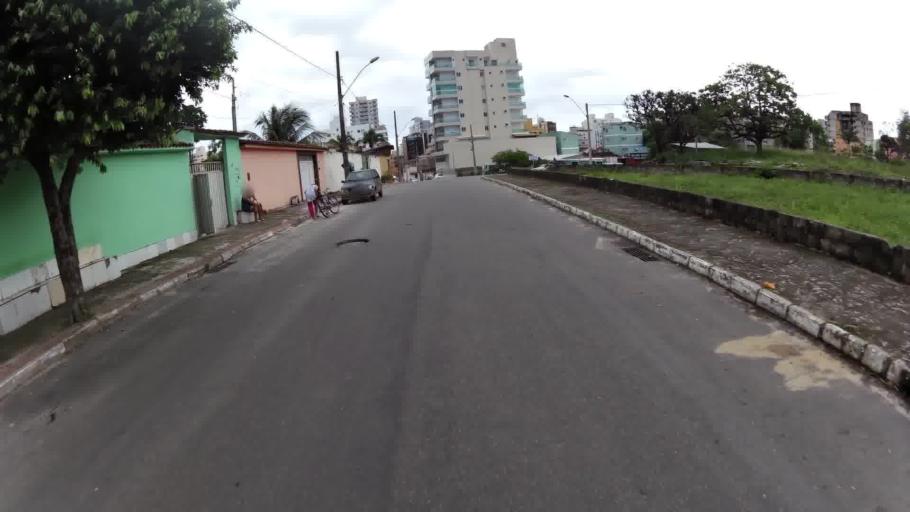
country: BR
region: Espirito Santo
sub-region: Guarapari
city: Guarapari
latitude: -20.6522
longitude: -40.4924
